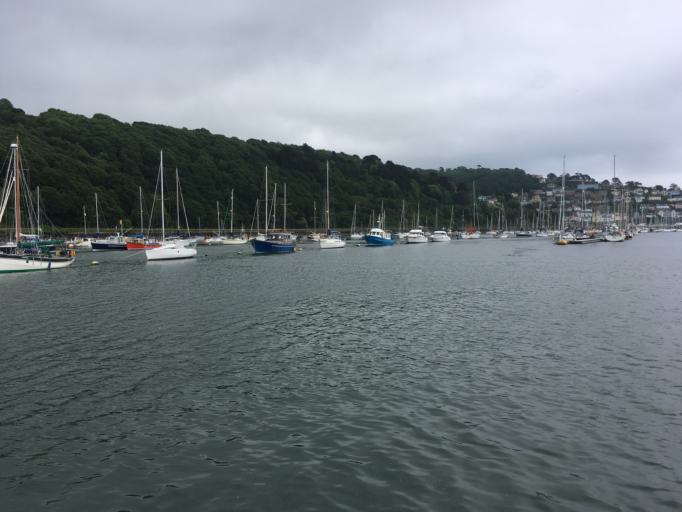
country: GB
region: England
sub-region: Devon
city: Dartmouth
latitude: 50.3580
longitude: -3.5753
